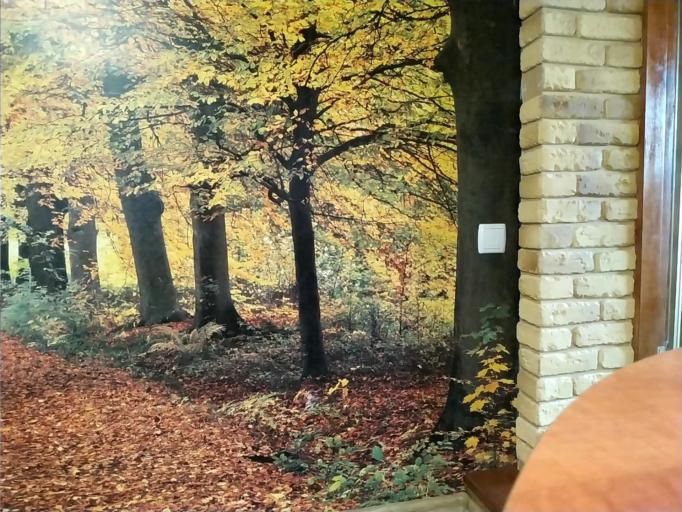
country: RU
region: Leningrad
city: Tolmachevo
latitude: 58.9331
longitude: 29.7065
